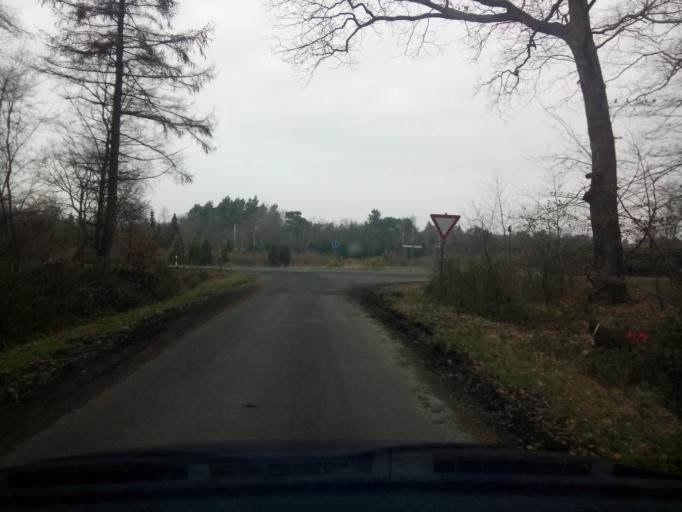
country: DE
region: Lower Saxony
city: Drangstedt
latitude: 53.6175
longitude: 8.7256
